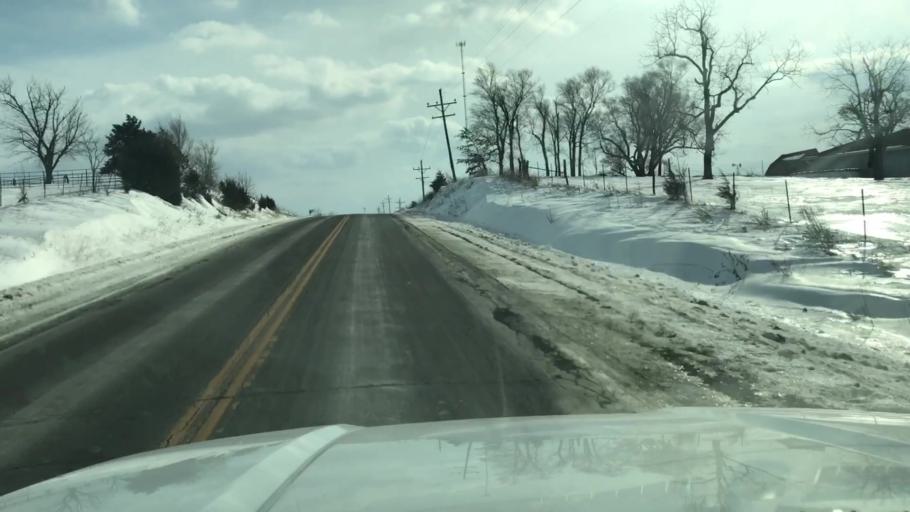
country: US
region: Missouri
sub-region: Gentry County
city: Stanberry
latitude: 40.3748
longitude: -94.6473
